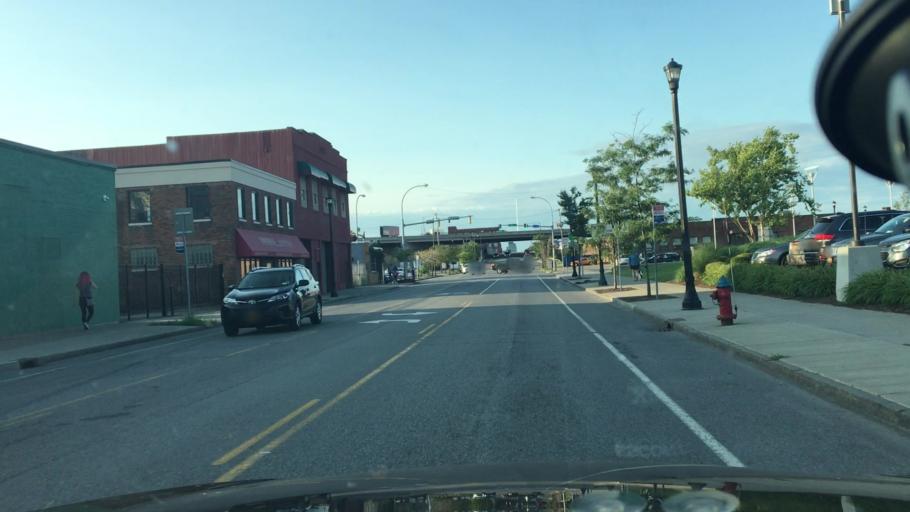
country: US
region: New York
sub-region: Erie County
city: Buffalo
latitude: 42.8741
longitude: -78.8714
